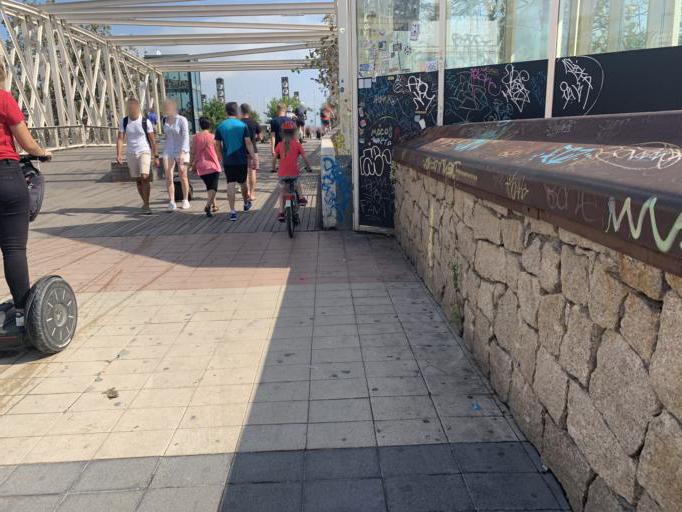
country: ES
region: Catalonia
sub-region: Provincia de Barcelona
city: Ciutat Vella
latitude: 41.3856
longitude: 2.1973
